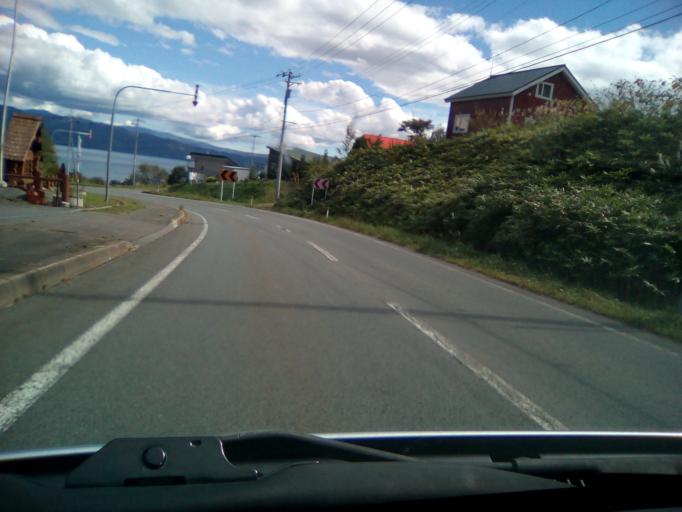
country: JP
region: Hokkaido
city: Date
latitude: 42.6457
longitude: 140.8232
